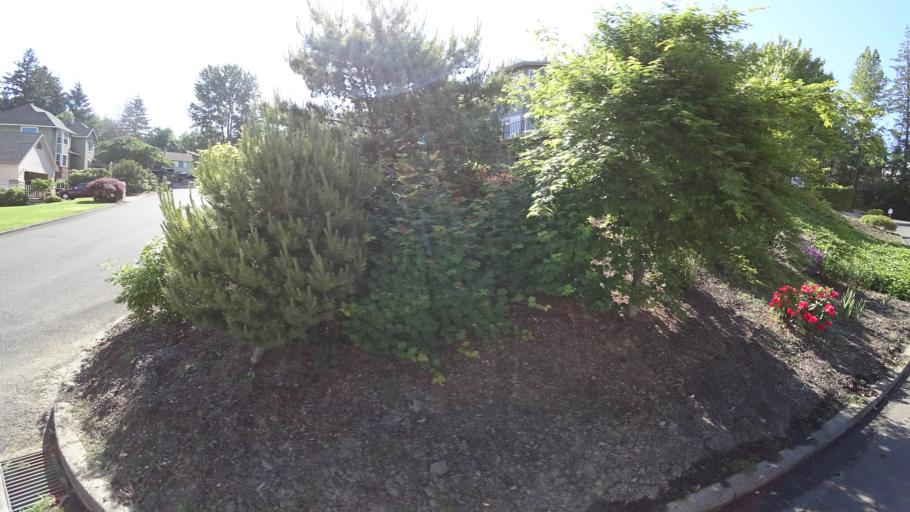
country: US
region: Oregon
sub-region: Multnomah County
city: Lents
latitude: 45.4652
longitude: -122.5526
